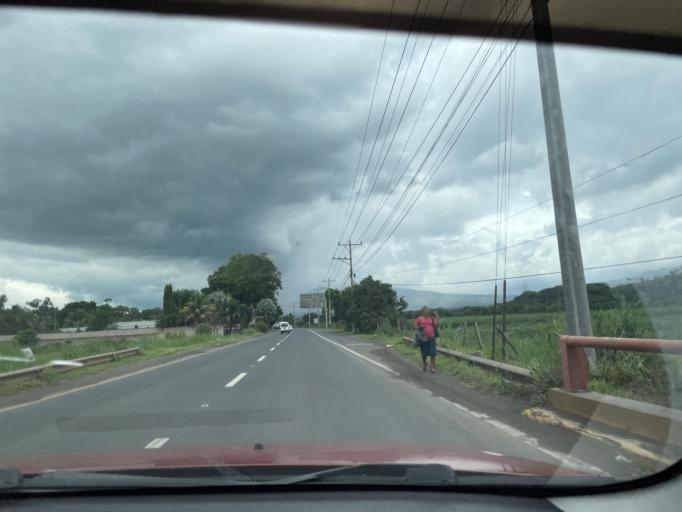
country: SV
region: Sonsonate
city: Armenia
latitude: 13.7397
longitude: -89.4260
